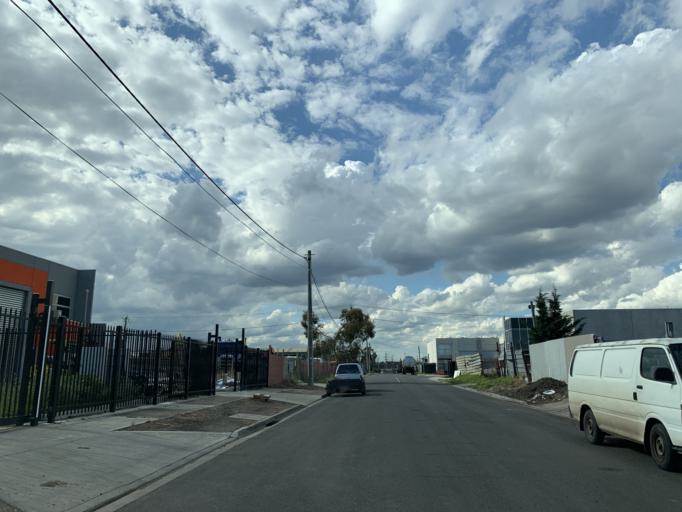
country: AU
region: Victoria
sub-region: Brimbank
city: Albion
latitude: -37.7524
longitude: 144.8395
